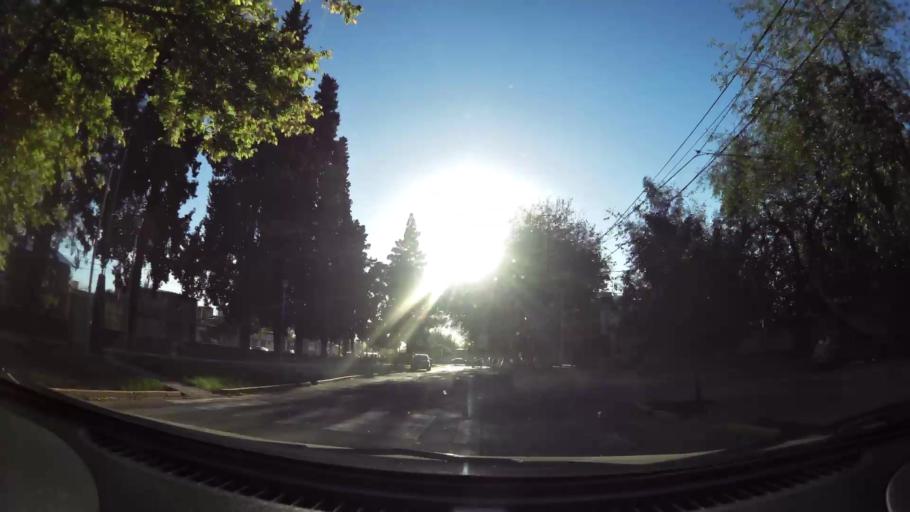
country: AR
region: Mendoza
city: Las Heras
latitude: -32.8623
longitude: -68.8336
